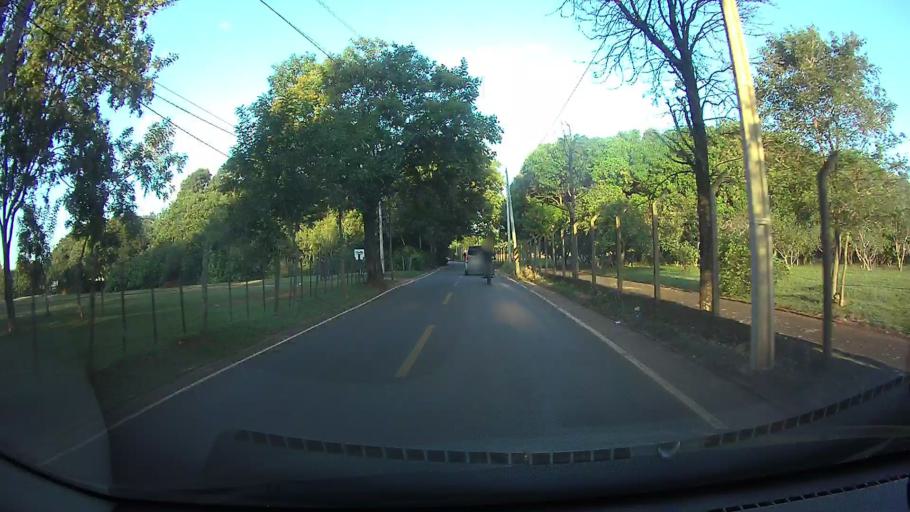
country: PY
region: Central
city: San Lorenzo
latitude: -25.2868
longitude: -57.5089
